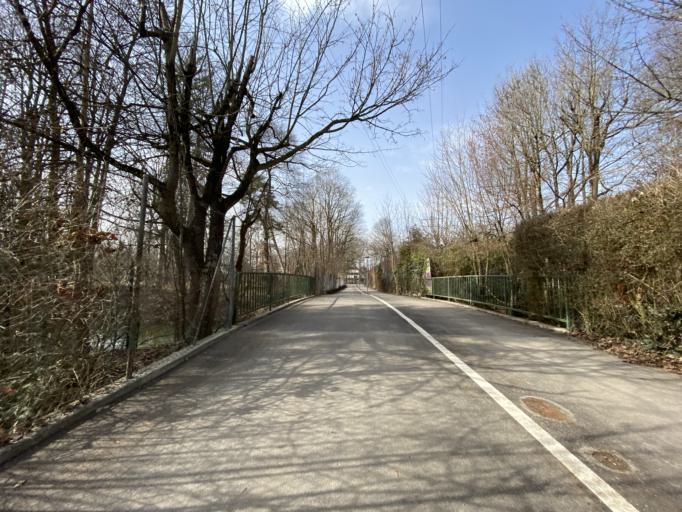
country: DE
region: Bavaria
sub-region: Upper Bavaria
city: Unterfoehring
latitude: 48.1941
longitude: 11.6249
